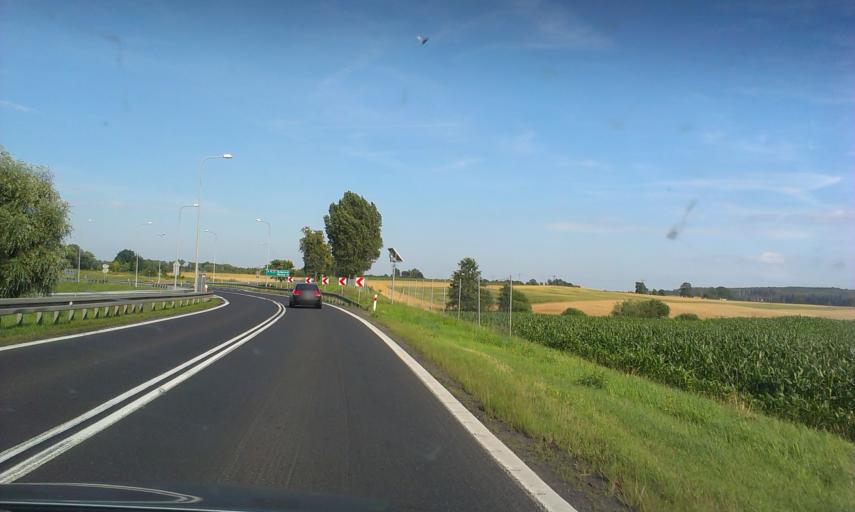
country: PL
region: Greater Poland Voivodeship
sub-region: Powiat pilski
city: Wyrzysk
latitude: 53.1615
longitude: 17.2039
